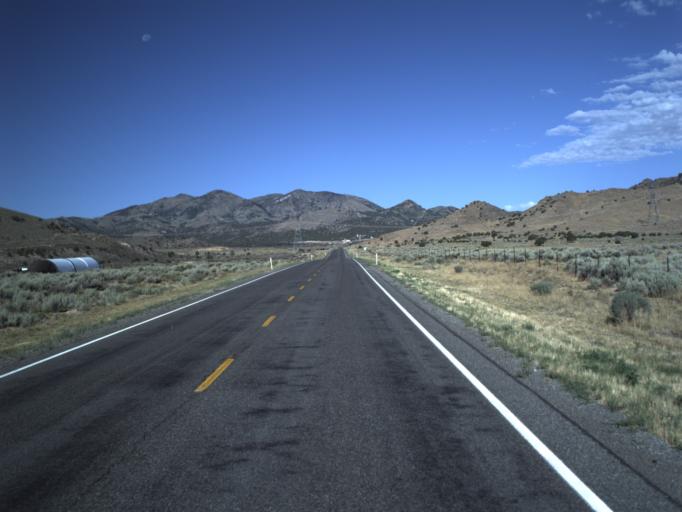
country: US
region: Utah
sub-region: Utah County
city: Genola
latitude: 39.9512
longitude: -111.9990
